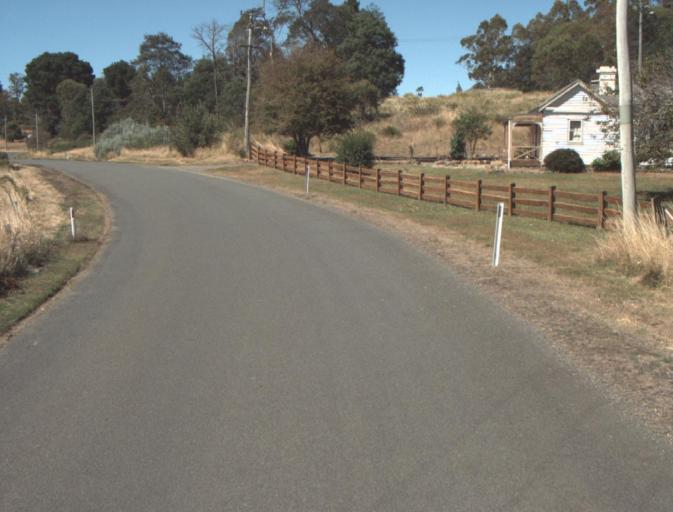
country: AU
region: Tasmania
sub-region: Launceston
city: Newstead
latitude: -41.3885
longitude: 147.2965
